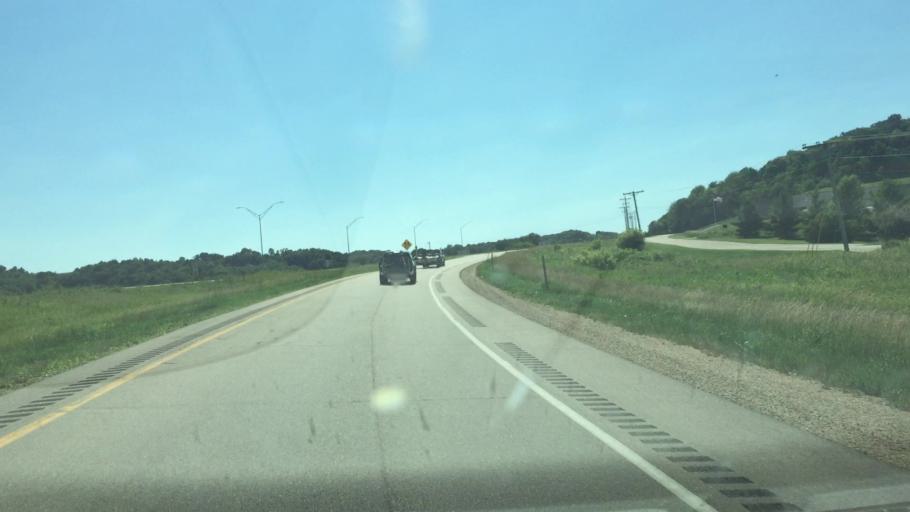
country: US
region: Iowa
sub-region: Dubuque County
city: Dubuque
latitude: 42.4196
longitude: -90.6971
